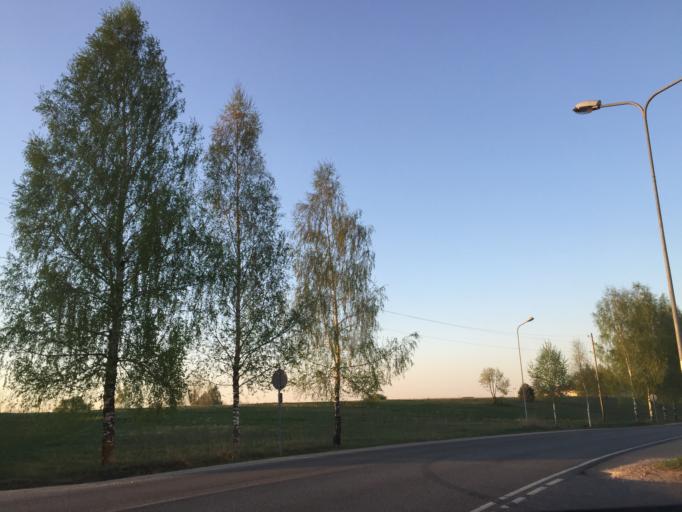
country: LV
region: Ikskile
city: Ikskile
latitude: 56.8647
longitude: 24.5616
